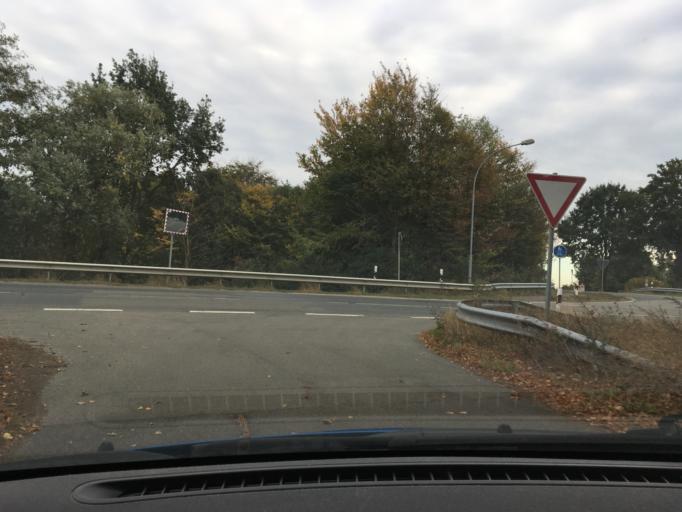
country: DE
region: Lower Saxony
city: Winsen
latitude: 53.3772
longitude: 10.2454
